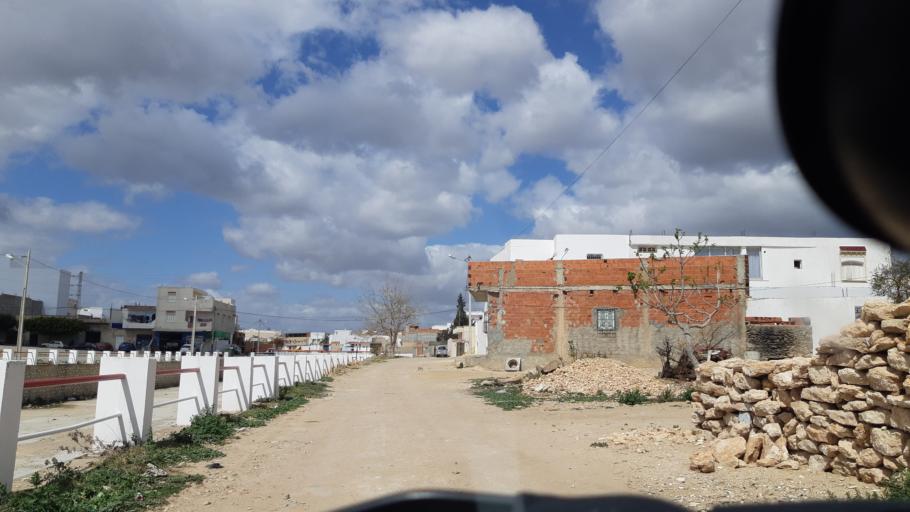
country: TN
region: Susah
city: Akouda
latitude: 35.8735
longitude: 10.5432
